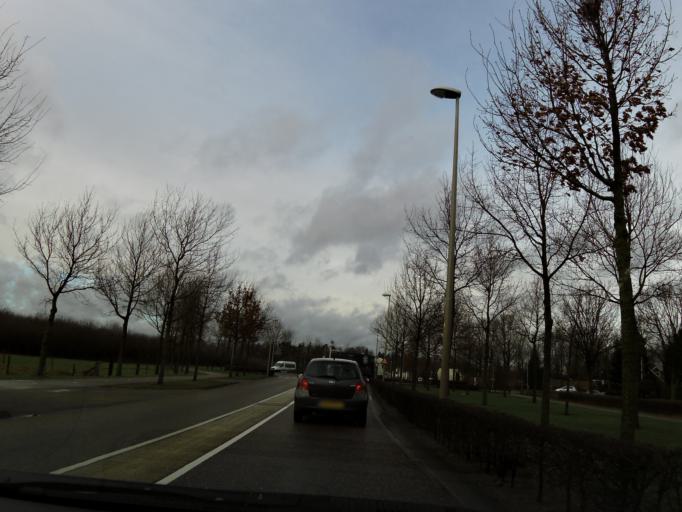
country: NL
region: Limburg
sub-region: Gemeente Roerdalen
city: Melick
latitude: 51.1598
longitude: 6.0078
